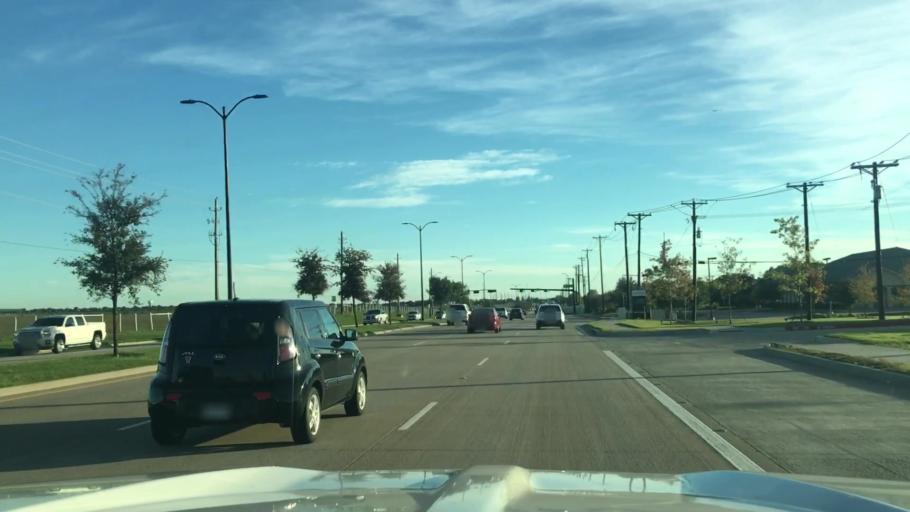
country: US
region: Texas
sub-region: Collin County
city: Frisco
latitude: 33.1651
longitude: -96.8033
